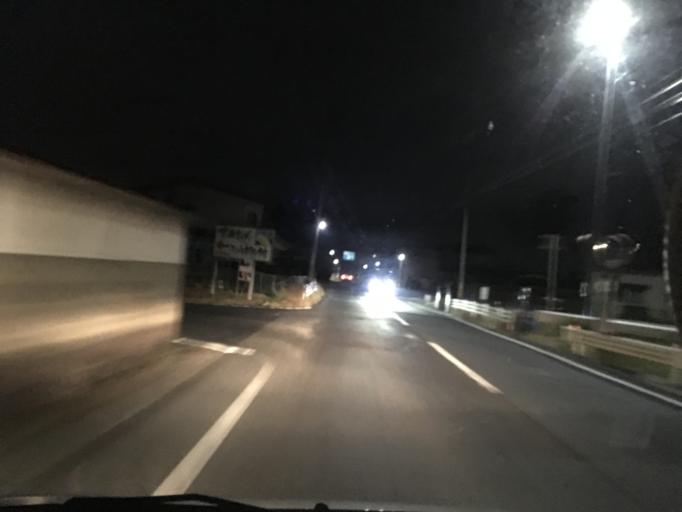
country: JP
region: Miyagi
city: Wakuya
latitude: 38.7173
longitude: 141.2149
